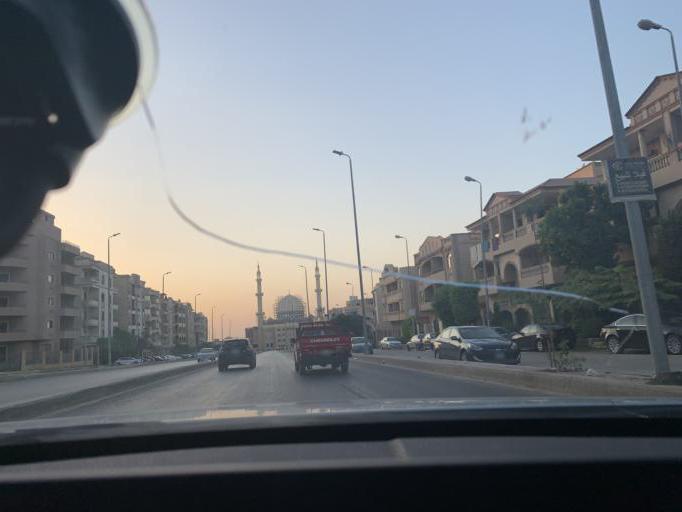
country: EG
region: Muhafazat al Qahirah
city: Cairo
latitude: 30.0031
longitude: 31.4595
